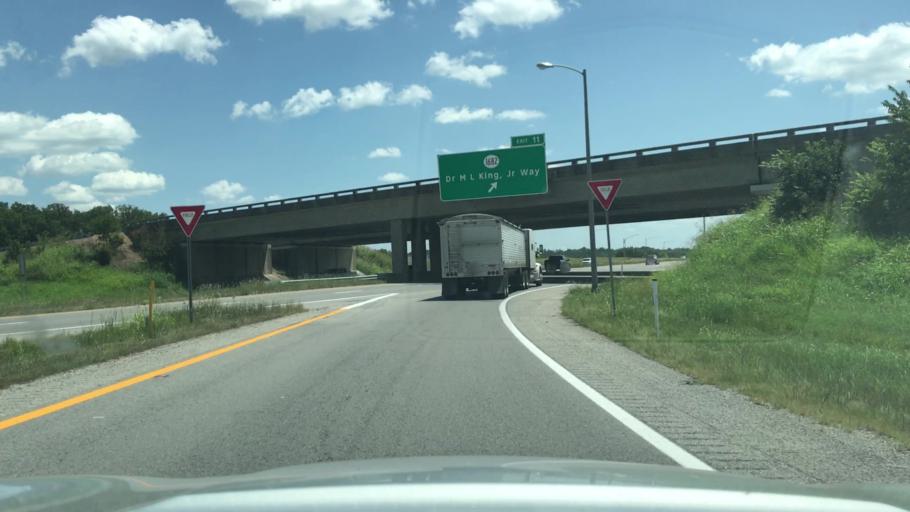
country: US
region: Kentucky
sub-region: Christian County
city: Hopkinsville
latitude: 36.8954
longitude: -87.4693
